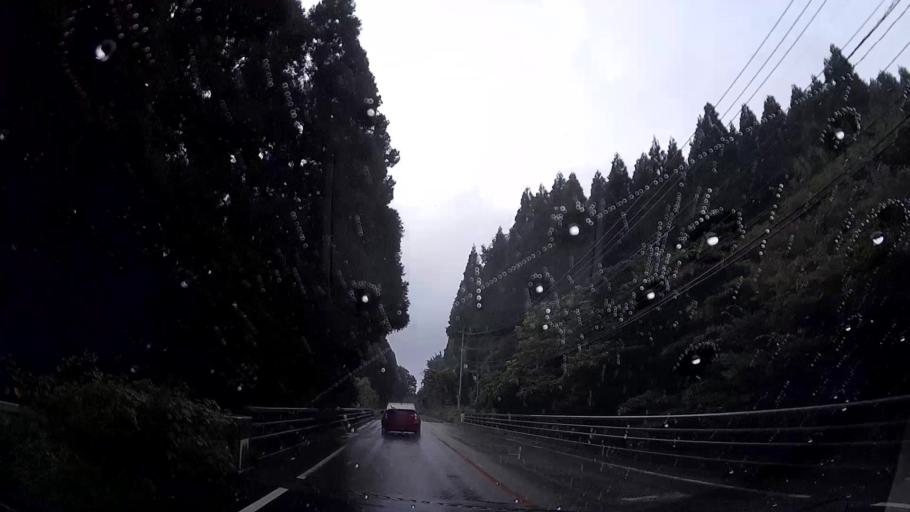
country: JP
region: Kumamoto
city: Aso
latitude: 32.8688
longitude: 130.9988
